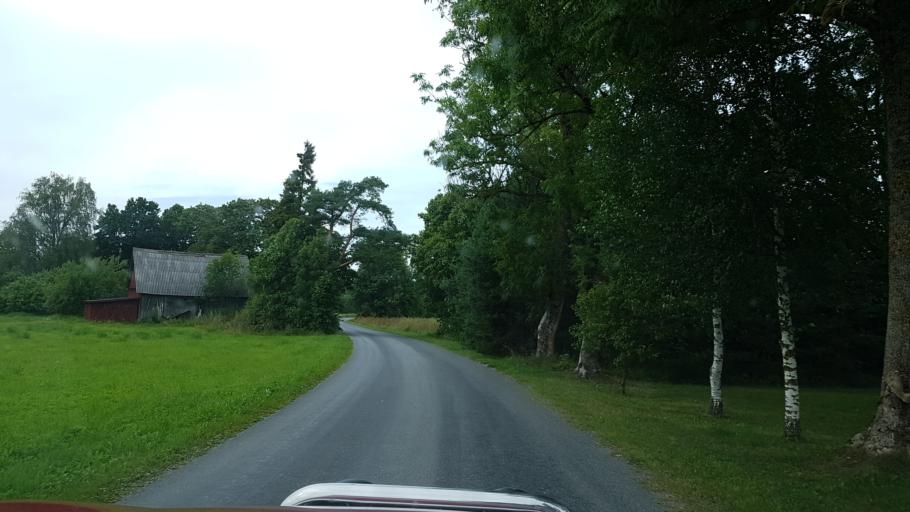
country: EE
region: Laeaene
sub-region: Ridala Parish
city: Uuemoisa
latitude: 59.0135
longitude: 23.7228
